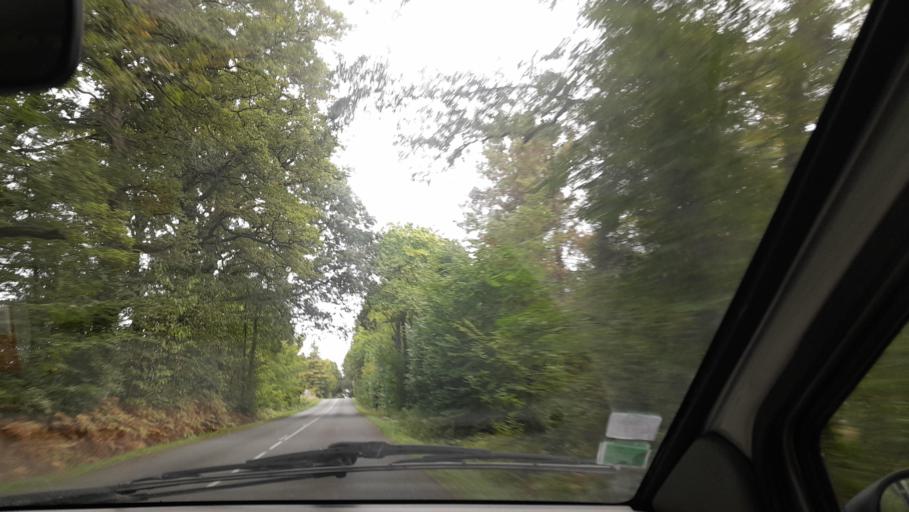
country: FR
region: Pays de la Loire
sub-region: Departement de Maine-et-Loire
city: Pouance
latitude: 47.7076
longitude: -1.1790
